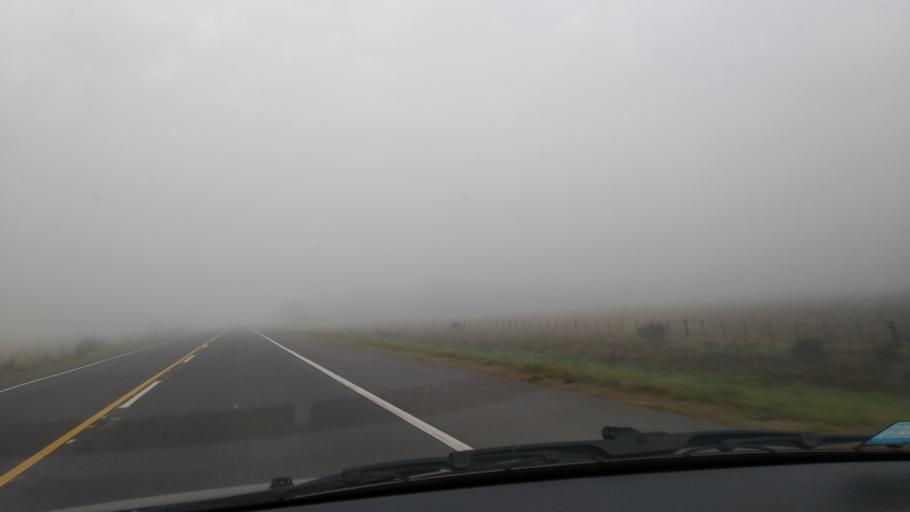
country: AR
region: Buenos Aires
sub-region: Partido de Brandsen
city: Brandsen
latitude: -35.1951
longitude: -58.3784
